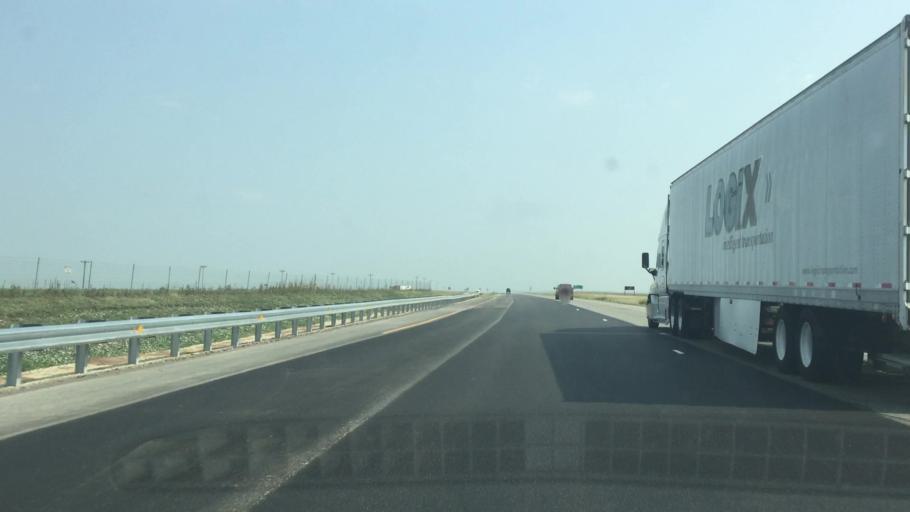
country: US
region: Kansas
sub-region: Chase County
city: Cottonwood Falls
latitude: 38.0991
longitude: -96.5767
